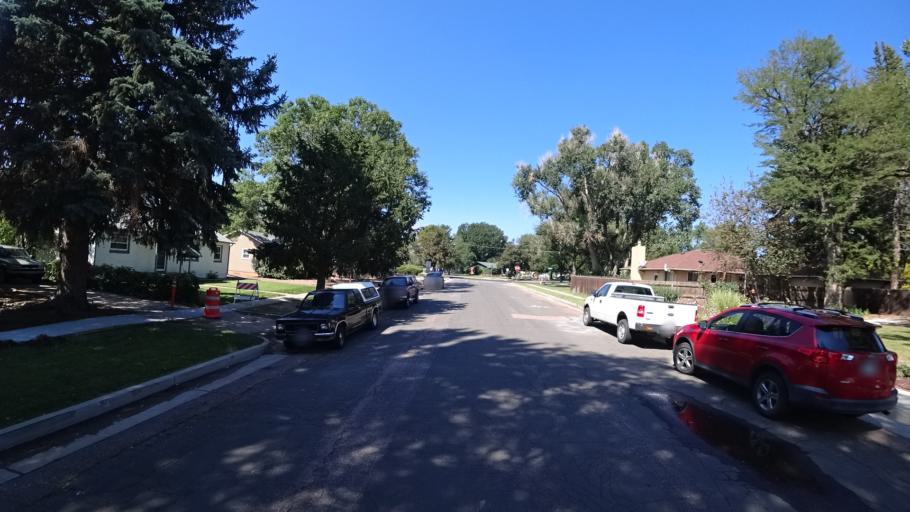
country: US
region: Colorado
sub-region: El Paso County
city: Colorado Springs
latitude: 38.8630
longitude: -104.8071
